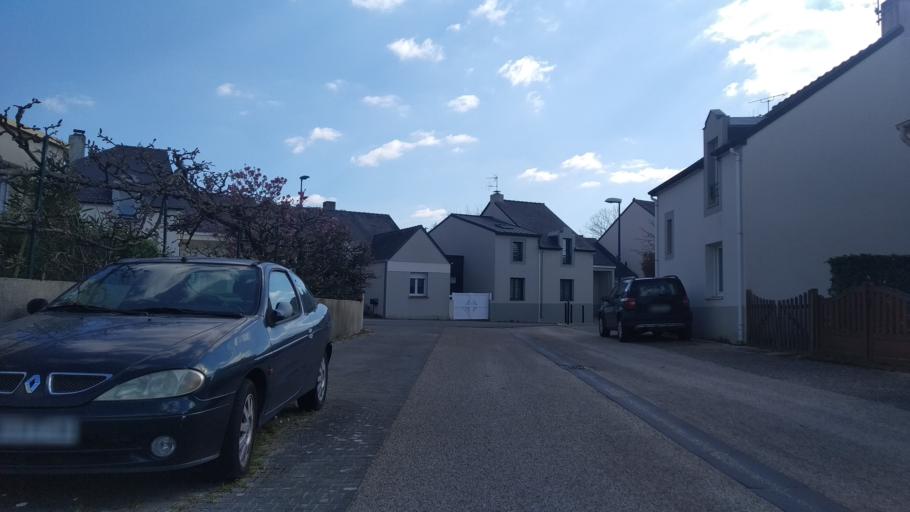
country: FR
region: Pays de la Loire
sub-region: Departement de la Loire-Atlantique
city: Sainte-Luce-sur-Loire
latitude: 47.2459
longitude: -1.5171
